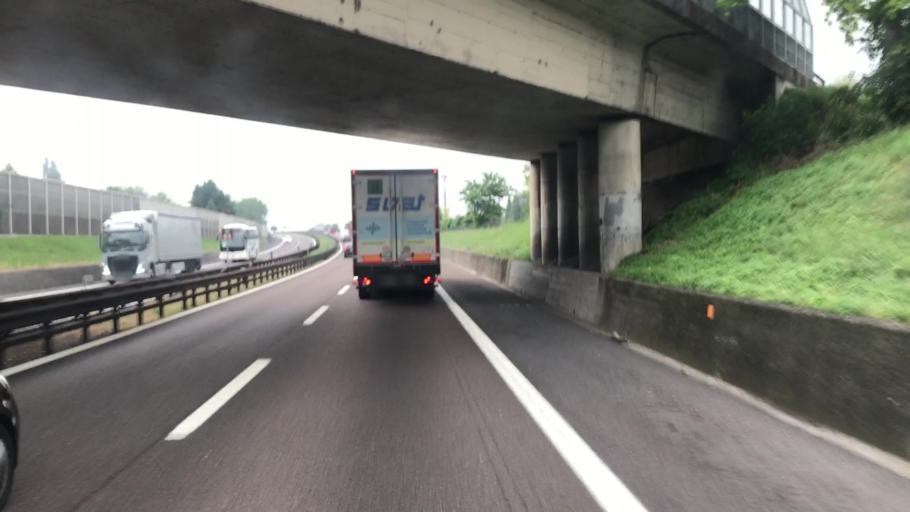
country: IT
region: Veneto
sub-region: Provincia di Verona
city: Dossobuono
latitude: 45.3932
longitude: 10.9085
